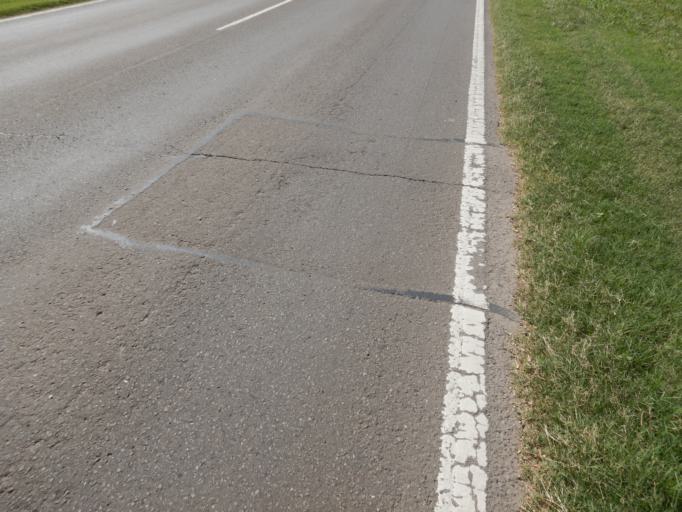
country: AR
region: Santa Fe
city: Carcarana
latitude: -32.8821
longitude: -61.0406
